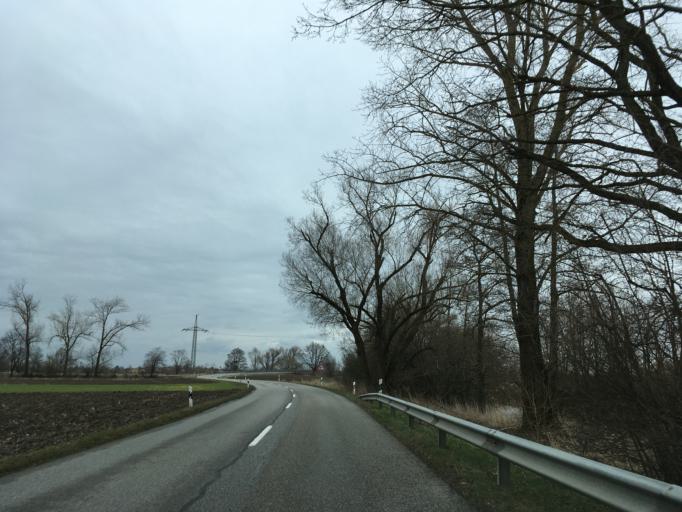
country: DE
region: Bavaria
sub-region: Upper Bavaria
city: Ampfing
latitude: 48.2593
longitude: 12.3844
